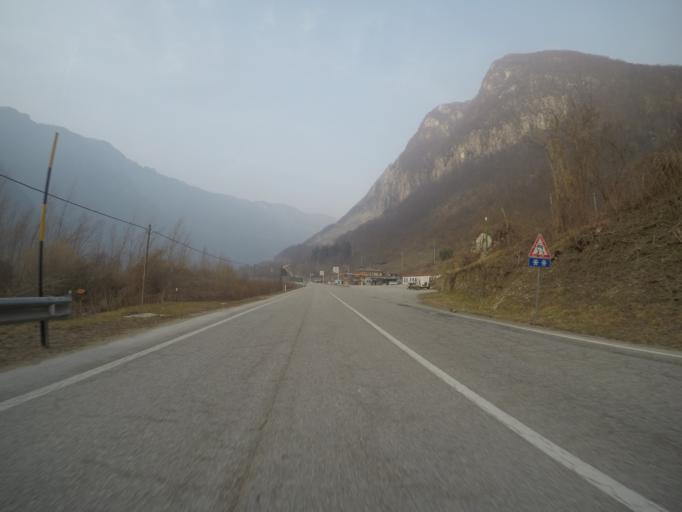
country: IT
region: Veneto
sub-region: Provincia di Belluno
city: Vas
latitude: 45.9605
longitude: 11.9386
